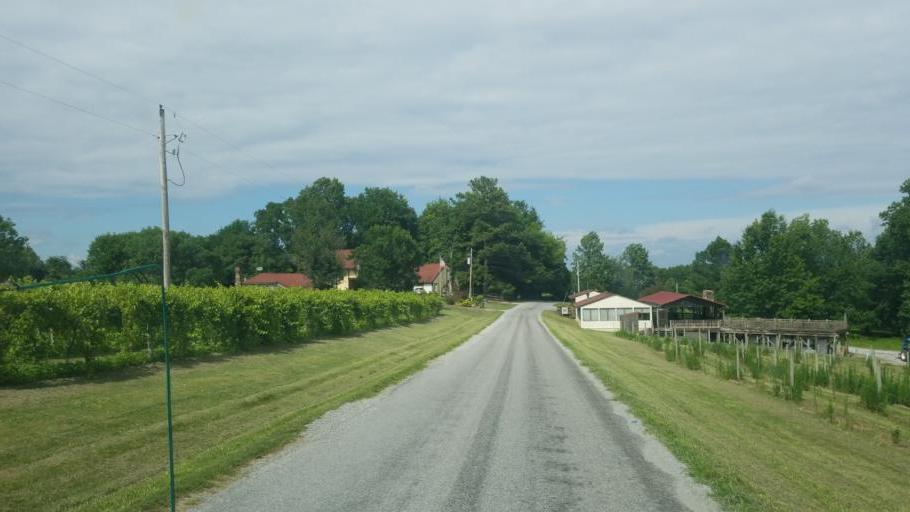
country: US
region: Illinois
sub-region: Union County
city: Cobden
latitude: 37.6124
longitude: -89.3520
